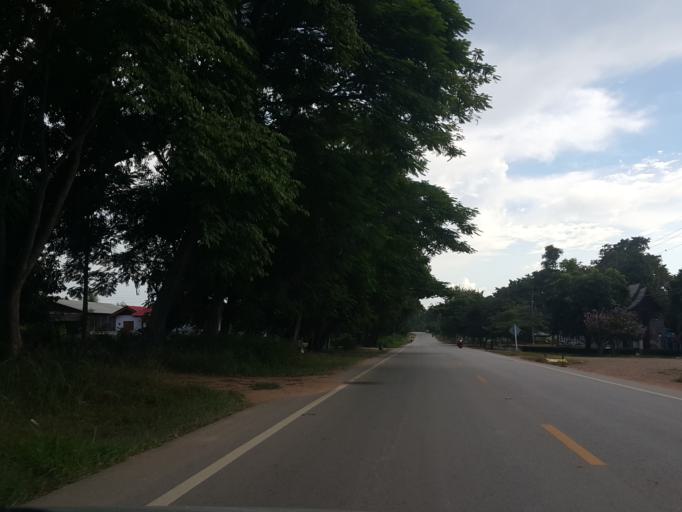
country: TH
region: Chiang Mai
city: Phrao
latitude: 19.3289
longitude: 99.1908
